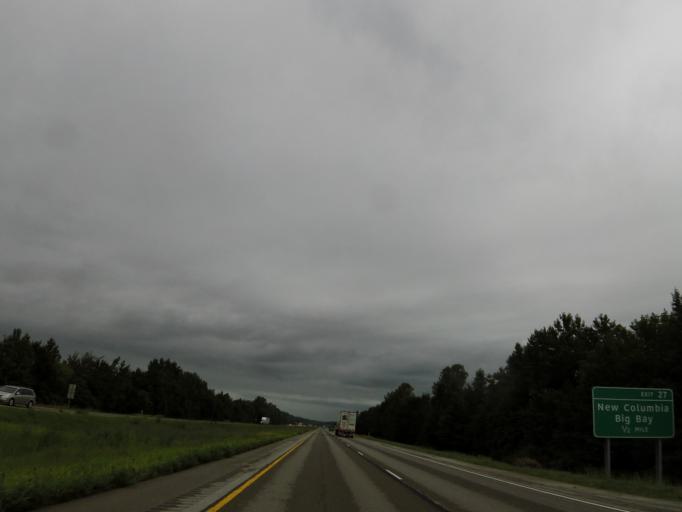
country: US
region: Illinois
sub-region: Massac County
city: Metropolis
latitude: 37.2897
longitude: -88.7492
